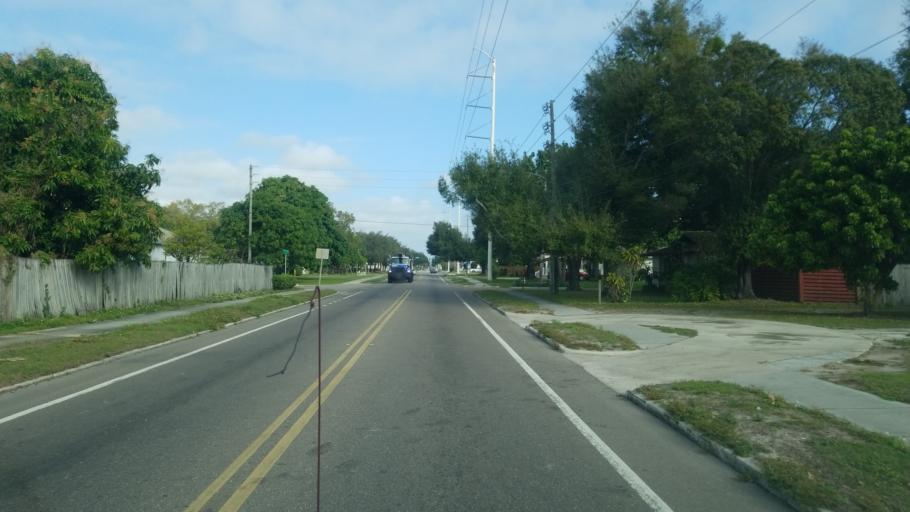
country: US
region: Florida
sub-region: Pinellas County
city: Lealman
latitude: 27.7968
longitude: -82.6713
